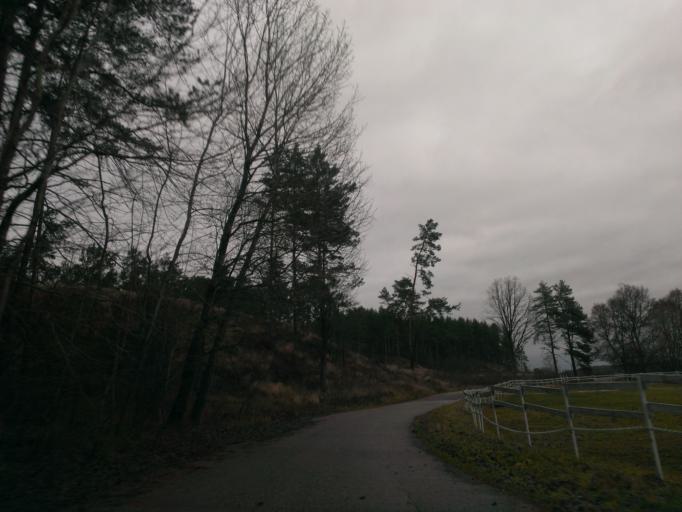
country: LV
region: Adazi
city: Adazi
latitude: 57.0600
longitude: 24.3546
